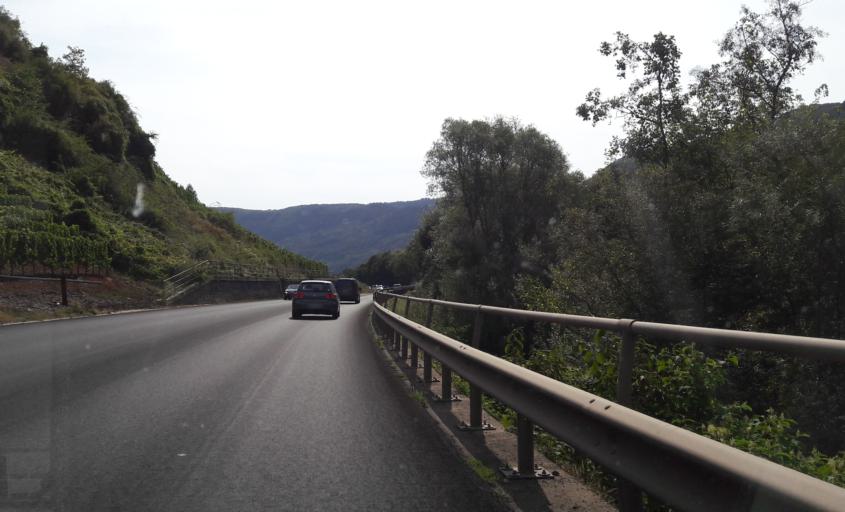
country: DE
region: Rheinland-Pfalz
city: Nehren
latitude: 50.0899
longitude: 7.1700
